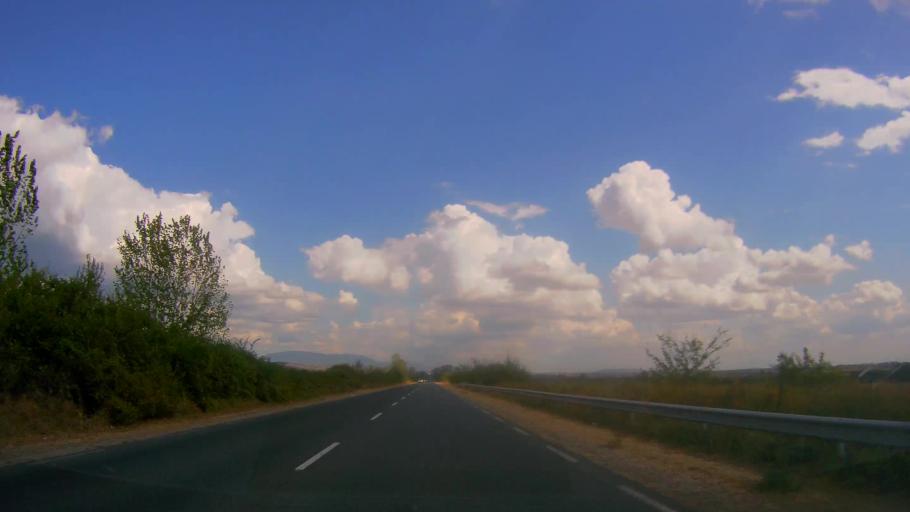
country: BG
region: Sliven
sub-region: Obshtina Sliven
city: Sliven
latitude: 42.6332
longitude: 26.2020
